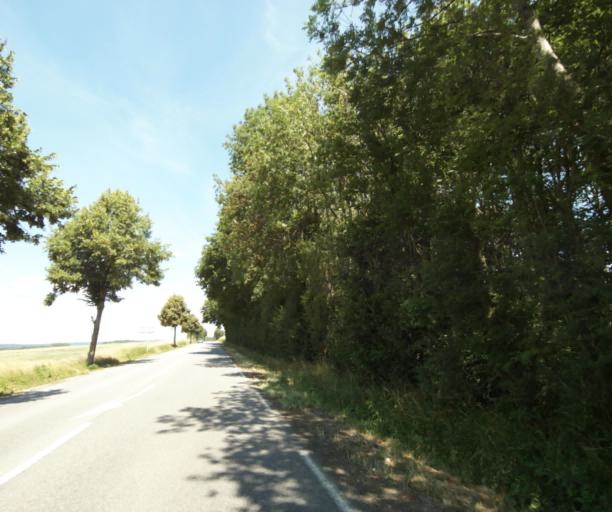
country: FR
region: Lorraine
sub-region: Departement de Meurthe-et-Moselle
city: Luneville
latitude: 48.6149
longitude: 6.4875
